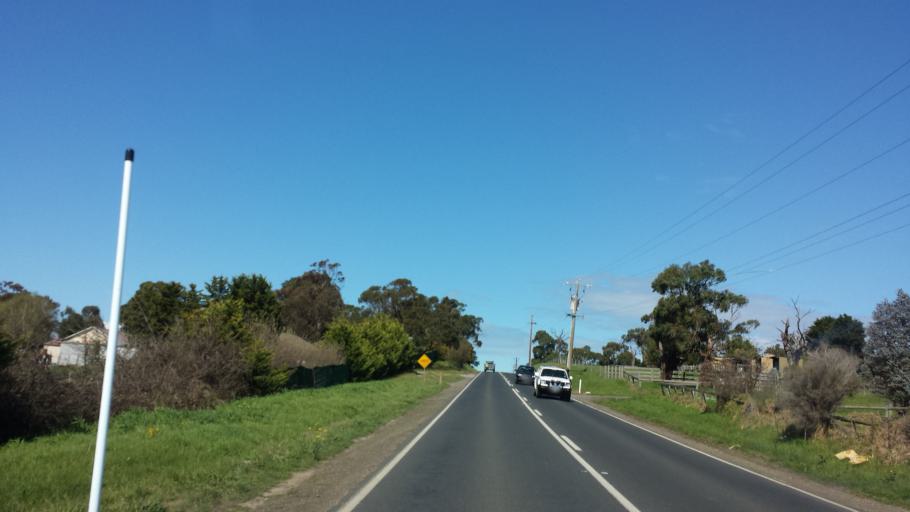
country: AU
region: Victoria
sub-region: Casey
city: Junction Village
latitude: -38.1409
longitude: 145.3227
